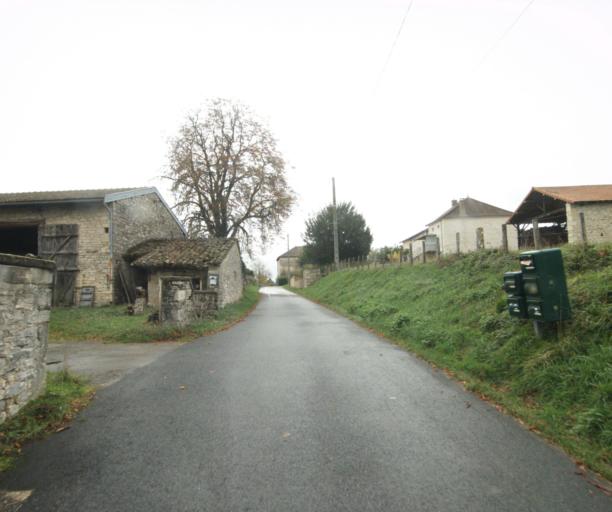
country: FR
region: Rhone-Alpes
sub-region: Departement de l'Ain
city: Pont-de-Vaux
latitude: 46.4698
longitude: 4.8859
